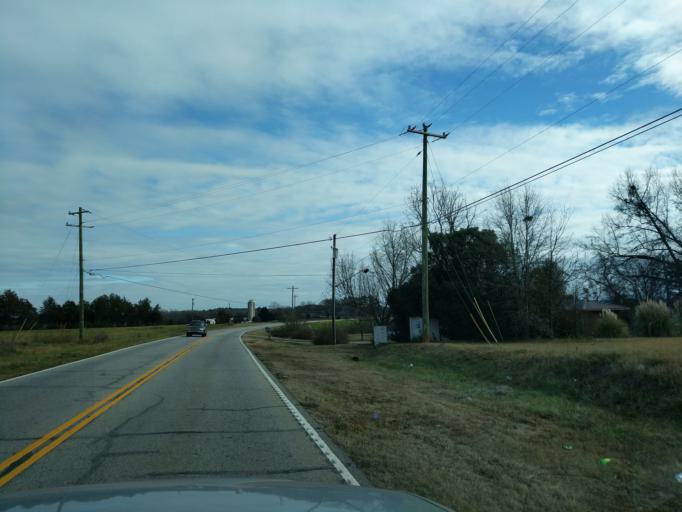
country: US
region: Georgia
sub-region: Hart County
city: Reed Creek
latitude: 34.5403
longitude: -82.8511
